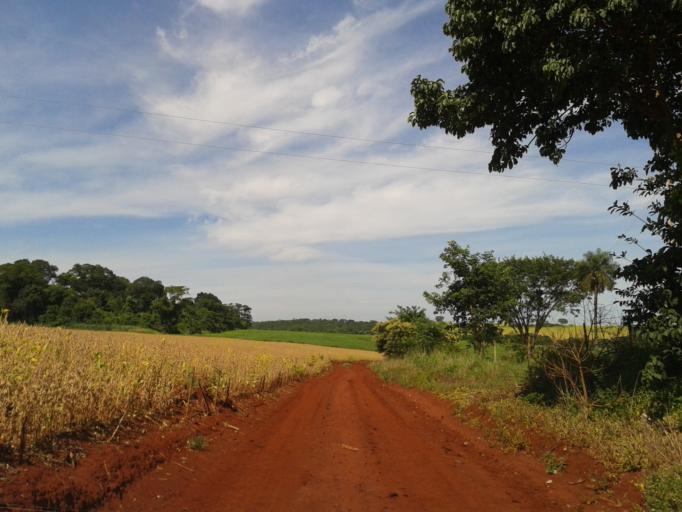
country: BR
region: Minas Gerais
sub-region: Capinopolis
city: Capinopolis
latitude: -18.6592
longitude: -49.7068
